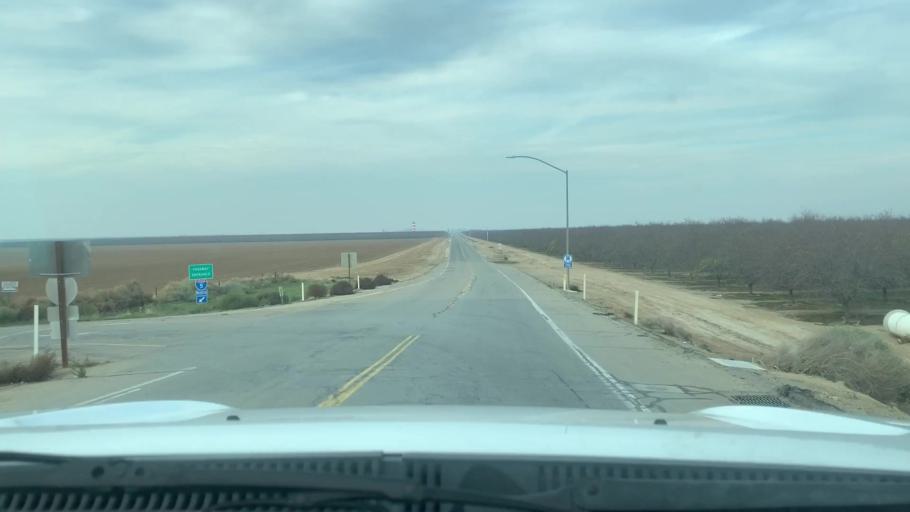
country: US
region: California
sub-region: Kern County
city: Buttonwillow
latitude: 35.4569
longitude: -119.4748
